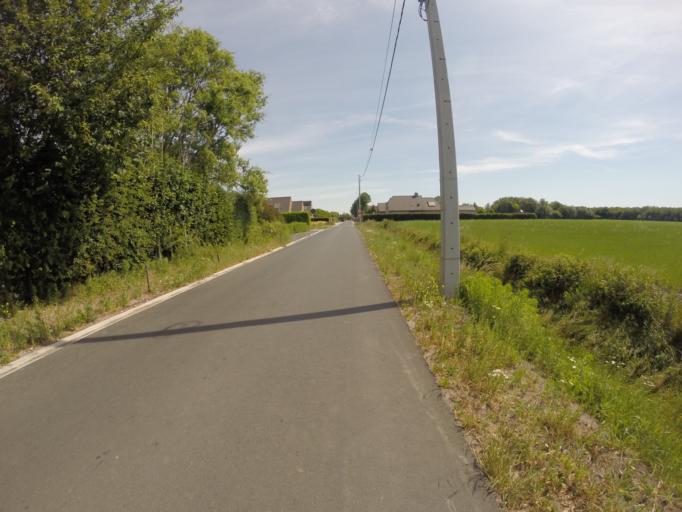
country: BE
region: Flanders
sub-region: Provincie Oost-Vlaanderen
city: Knesselare
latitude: 51.1421
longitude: 3.3819
